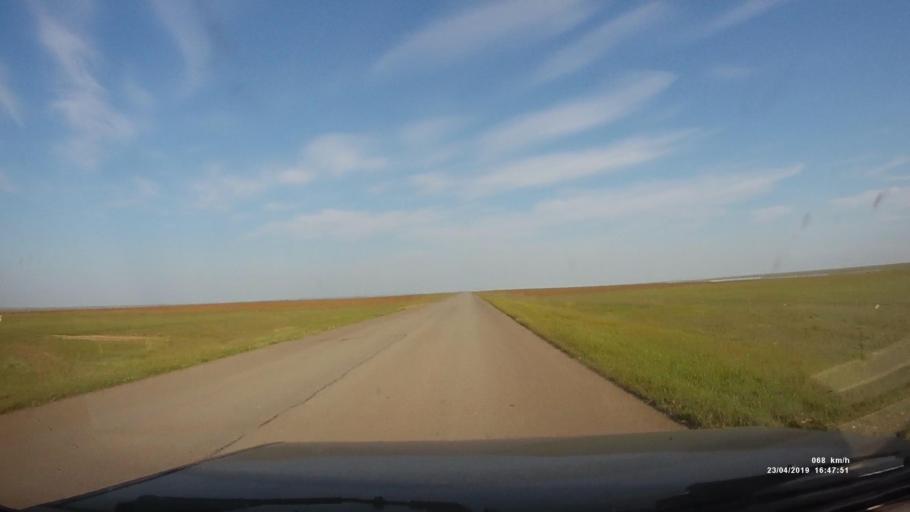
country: RU
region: Kalmykiya
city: Priyutnoye
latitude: 46.3373
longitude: 43.2534
